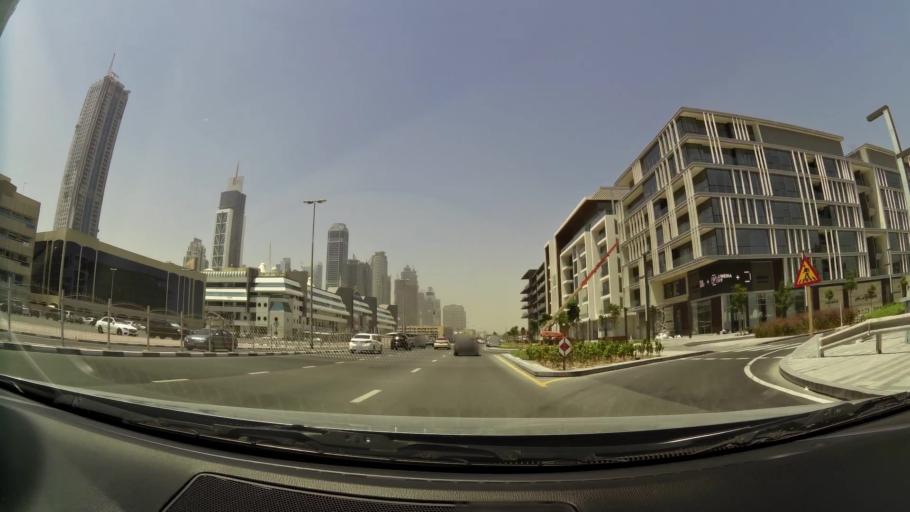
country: AE
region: Dubai
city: Dubai
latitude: 25.2013
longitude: 55.2658
